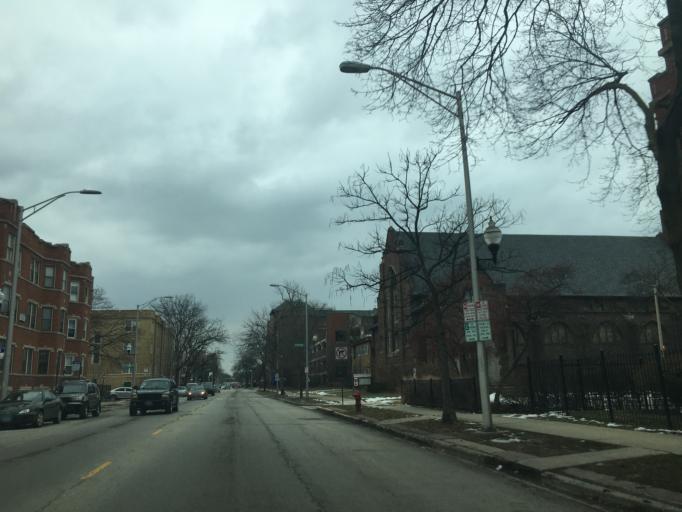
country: US
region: Illinois
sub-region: Cook County
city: Oak Park
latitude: 41.8935
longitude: -87.7751
